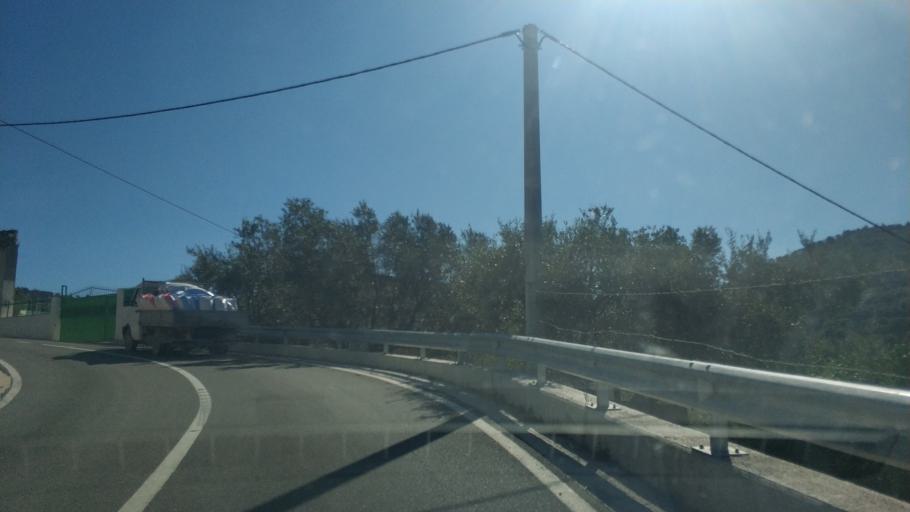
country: AL
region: Vlore
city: Vlore
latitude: 40.4573
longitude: 19.5055
